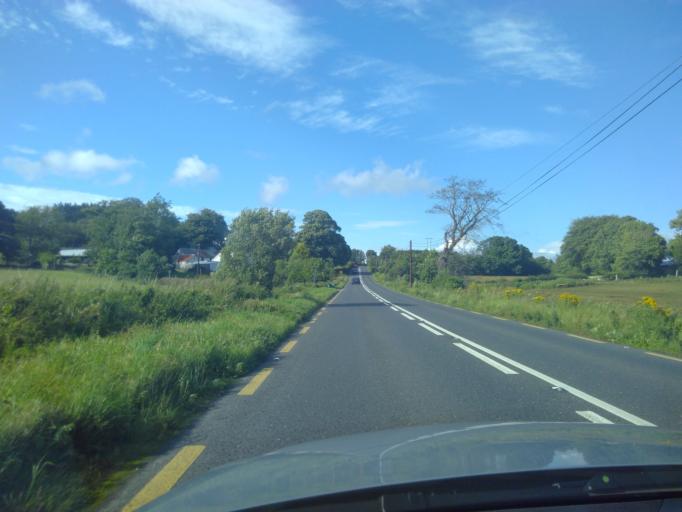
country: IE
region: Ulster
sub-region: County Donegal
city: Ballybofey
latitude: 54.8173
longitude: -7.7575
